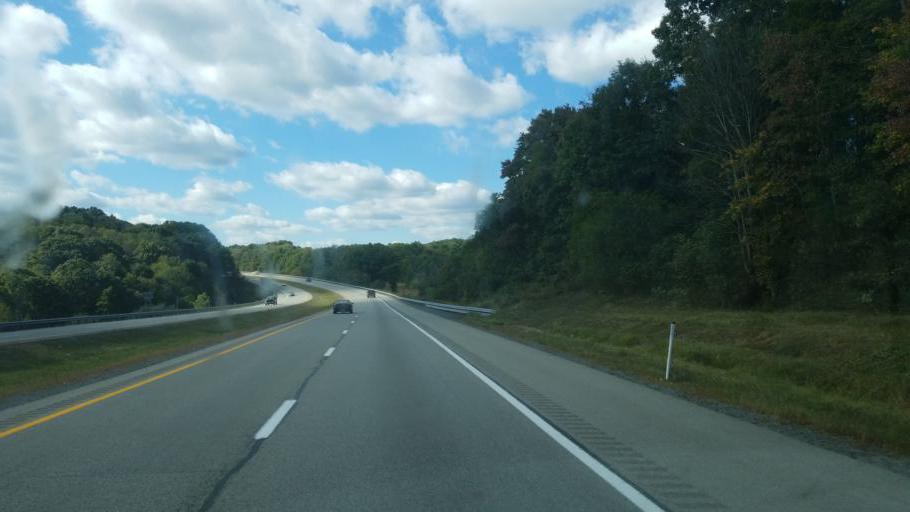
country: US
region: Pennsylvania
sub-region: Fayette County
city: Fairchance
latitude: 39.6605
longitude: -79.6631
